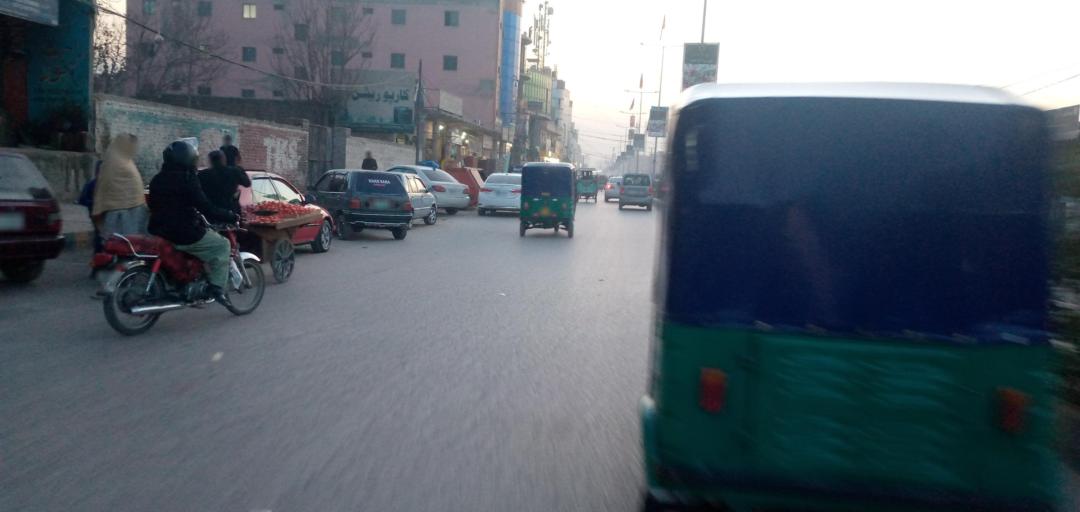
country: PK
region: Khyber Pakhtunkhwa
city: Peshawar
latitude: 34.0284
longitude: 71.6004
